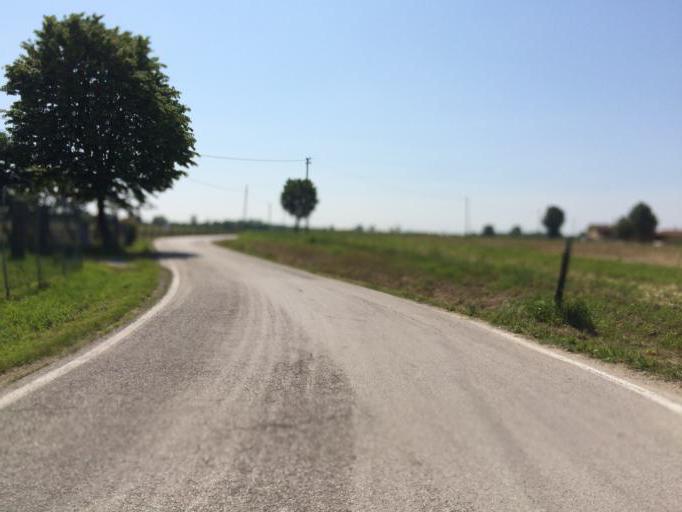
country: IT
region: Veneto
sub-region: Provincia di Vicenza
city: Montegalda
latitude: 45.4685
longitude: 11.6729
